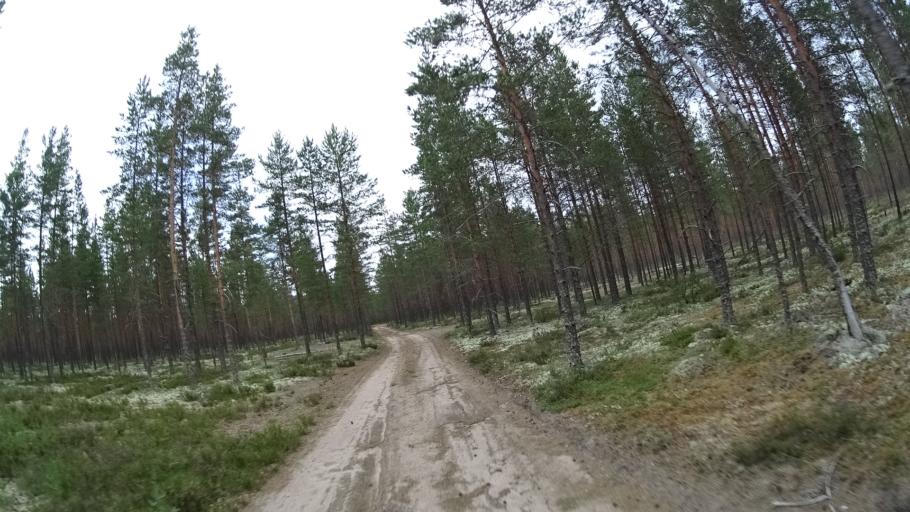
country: FI
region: Satakunta
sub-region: Pohjois-Satakunta
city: Jaemijaervi
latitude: 61.7647
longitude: 22.7867
